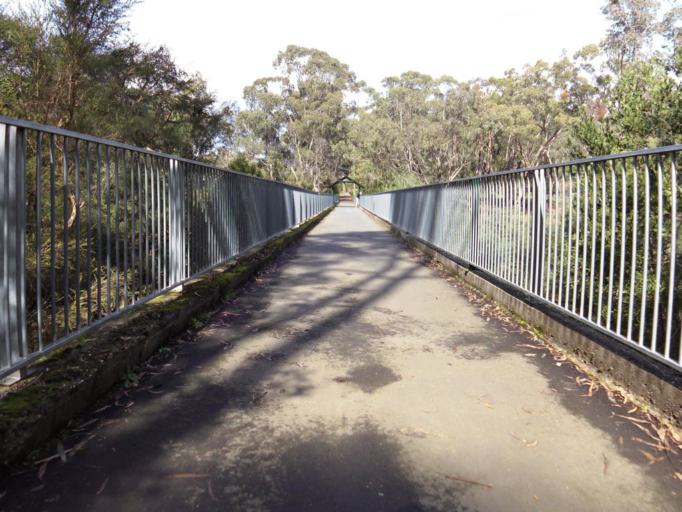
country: AU
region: Victoria
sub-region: Alpine
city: Mount Beauty
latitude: -36.7178
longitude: 146.9436
